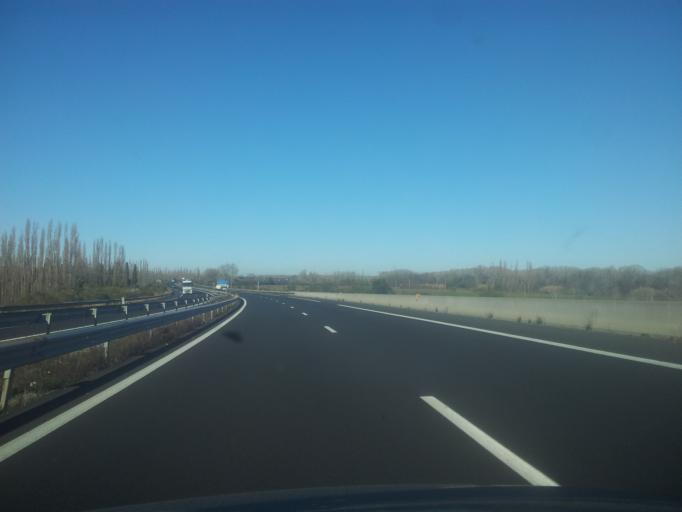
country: FR
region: Languedoc-Roussillon
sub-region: Departement du Gard
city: Roquemaure
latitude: 44.0579
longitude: 4.7680
